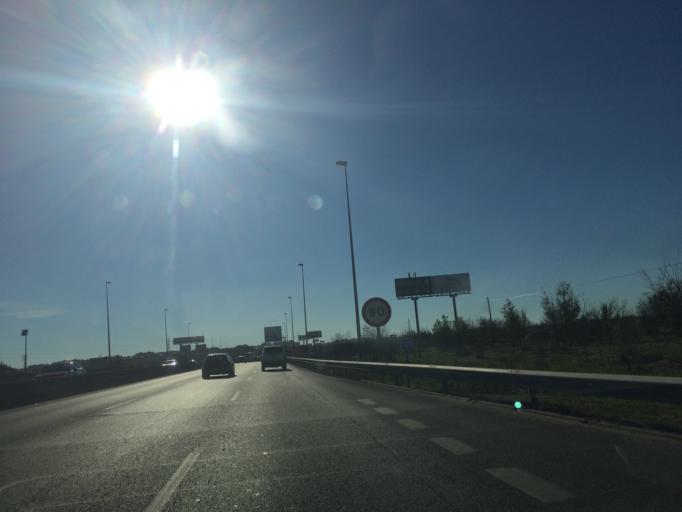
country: ES
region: Madrid
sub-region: Provincia de Madrid
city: Alcorcon
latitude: 40.3679
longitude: -3.8055
